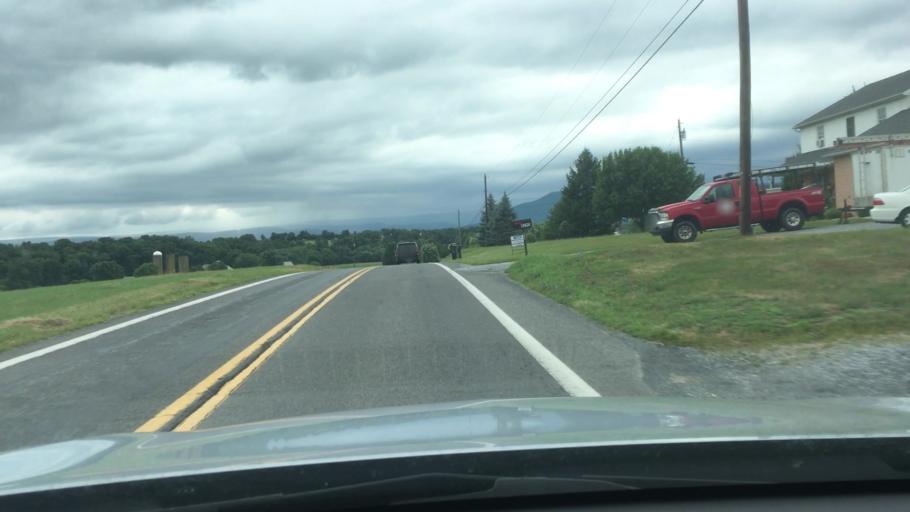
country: US
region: Pennsylvania
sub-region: Franklin County
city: Greencastle
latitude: 39.8671
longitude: -77.7775
